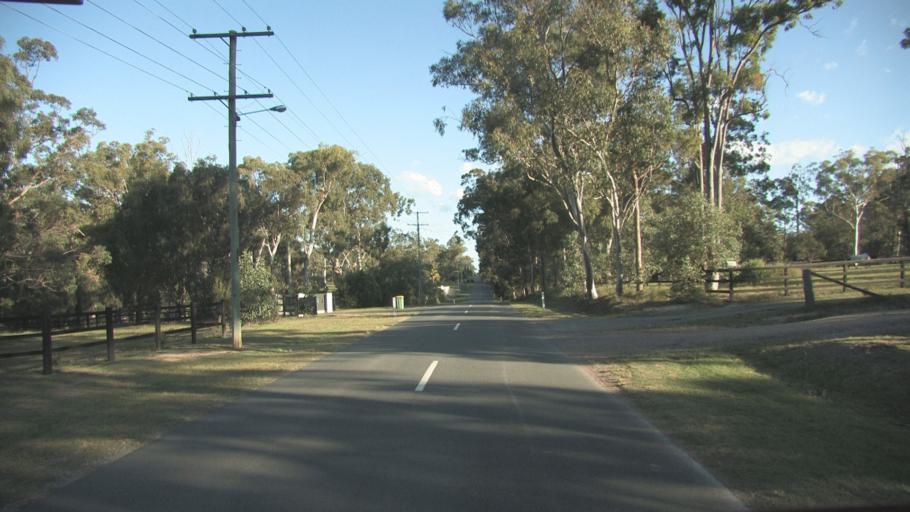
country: AU
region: Queensland
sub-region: Redland
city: Redland Bay
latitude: -27.6749
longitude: 153.2762
